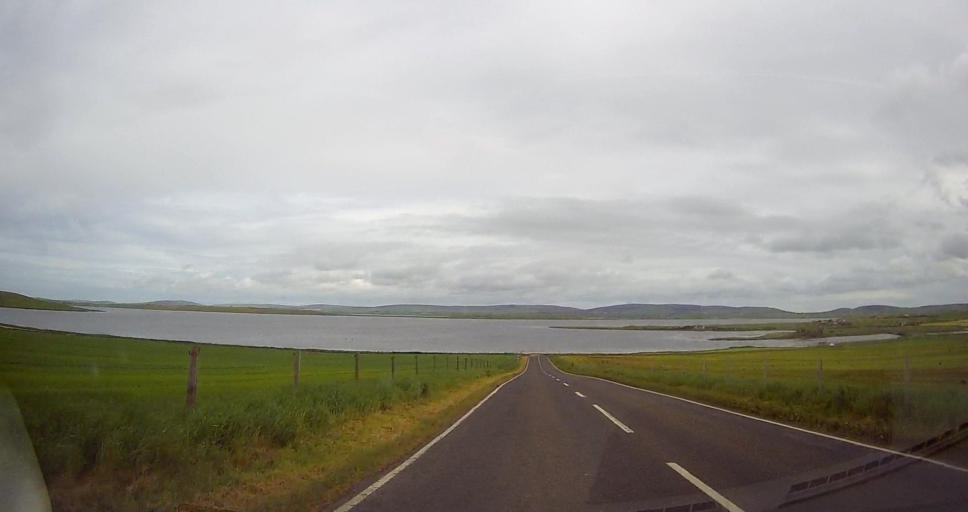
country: GB
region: Scotland
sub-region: Orkney Islands
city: Stromness
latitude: 58.9811
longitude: -3.2622
